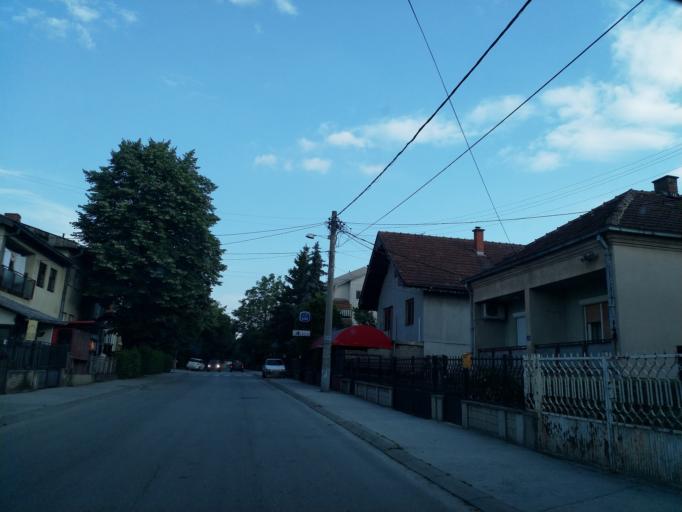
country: RS
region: Central Serbia
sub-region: Pomoravski Okrug
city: Jagodina
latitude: 43.9802
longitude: 21.2459
